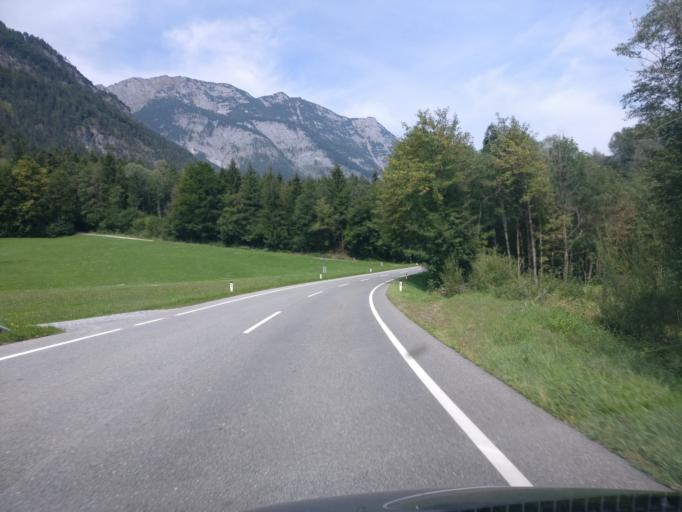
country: AT
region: Salzburg
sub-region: Politischer Bezirk Sankt Johann im Pongau
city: Werfen
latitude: 47.5065
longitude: 13.1666
